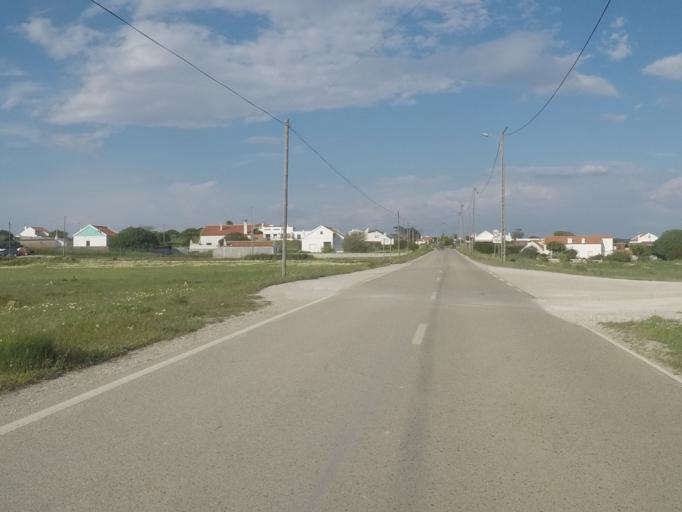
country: PT
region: Setubal
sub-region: Sesimbra
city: Sesimbra
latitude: 38.4259
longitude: -9.1932
